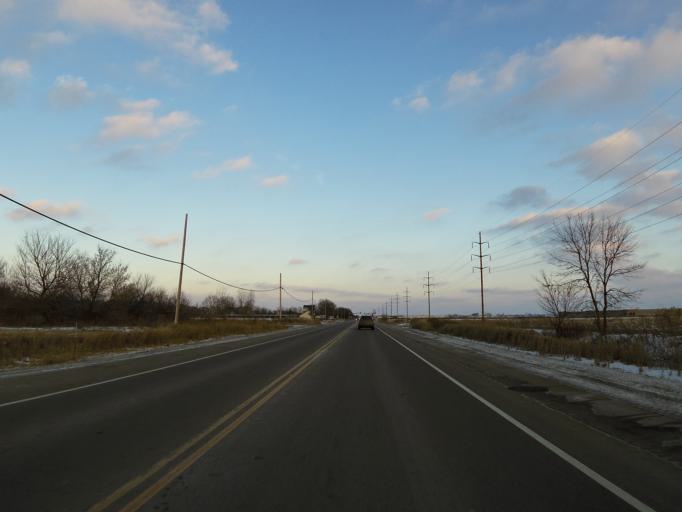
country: US
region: Minnesota
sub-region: Dakota County
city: Lakeville
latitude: 44.6379
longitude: -93.2616
